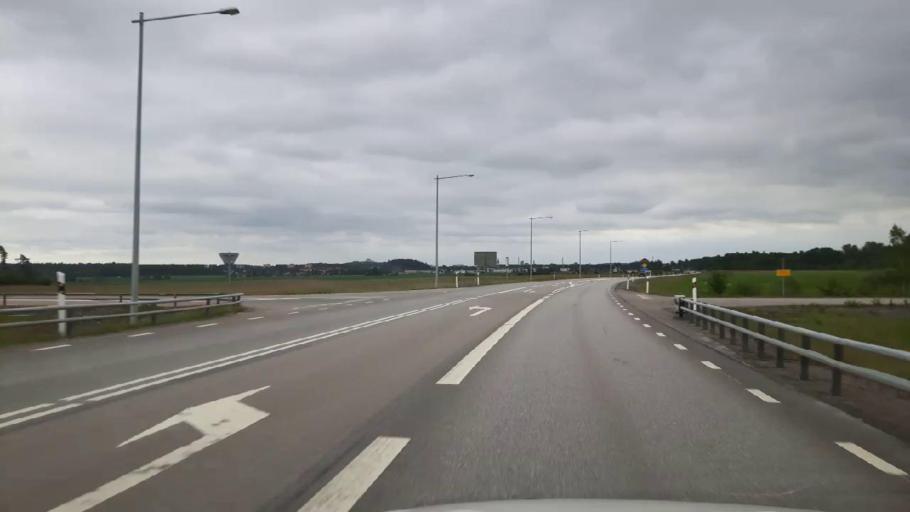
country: SE
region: Vaestmanland
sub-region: Kopings Kommun
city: Koping
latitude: 59.5358
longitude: 15.9530
